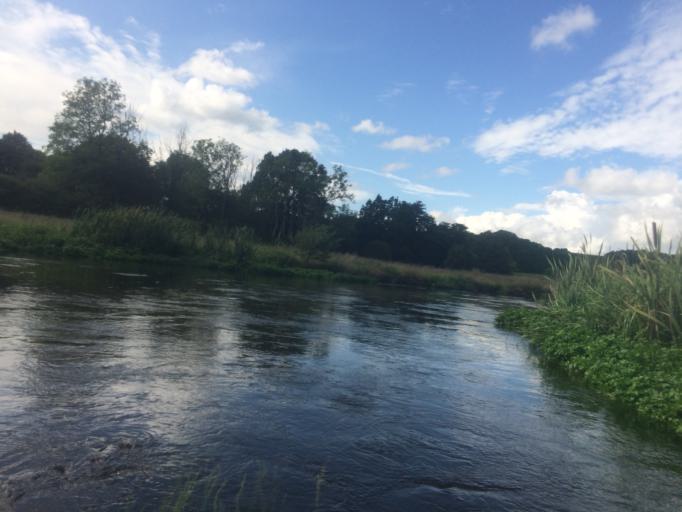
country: DK
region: South Denmark
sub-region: Vejle Kommune
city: Egtved
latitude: 55.6599
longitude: 9.3162
